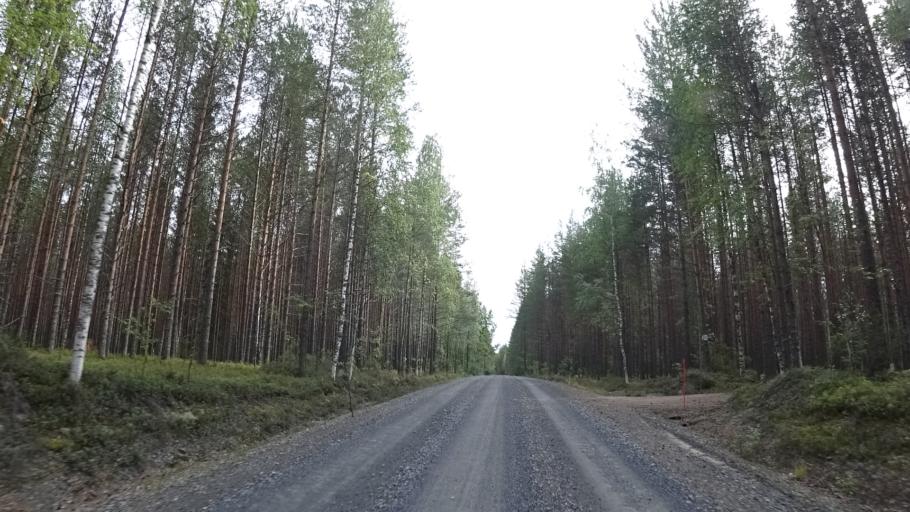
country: FI
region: North Karelia
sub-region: Joensuu
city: Ilomantsi
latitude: 62.6076
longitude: 31.1855
